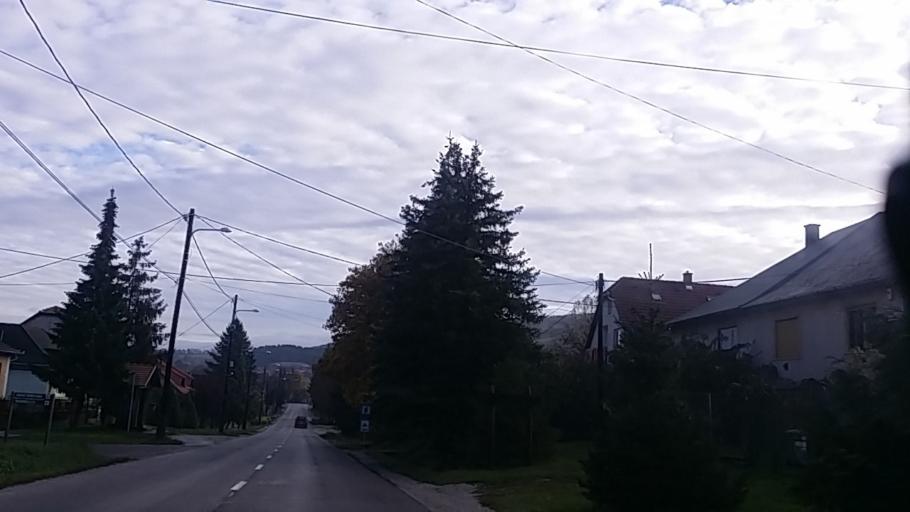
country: HU
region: Heves
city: Szilvasvarad
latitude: 48.0956
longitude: 20.3838
